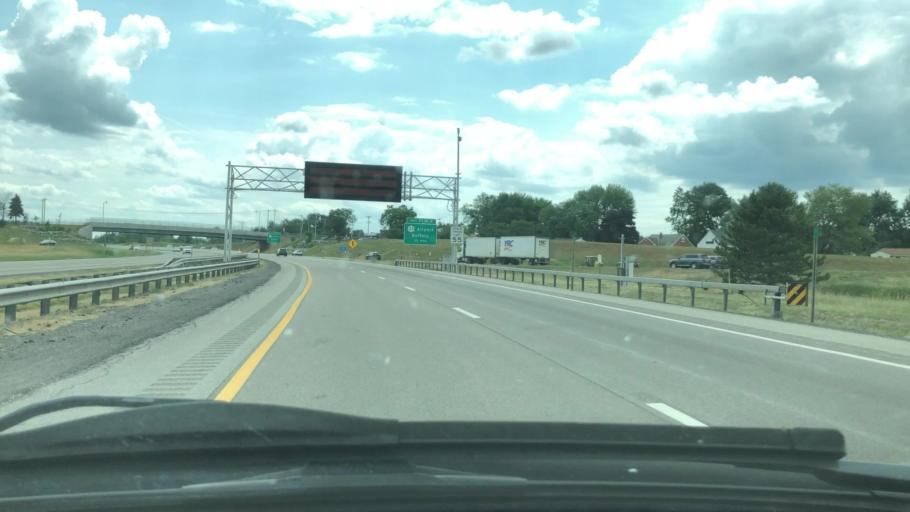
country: US
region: New York
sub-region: Erie County
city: Williamsville
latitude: 42.9479
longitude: -78.7650
